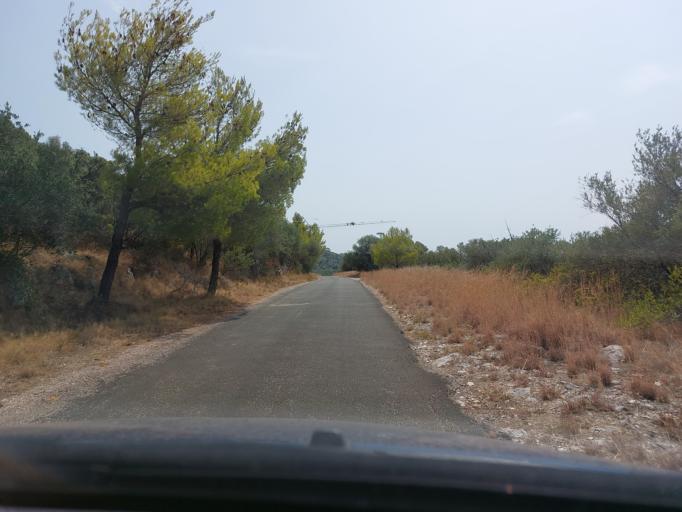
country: HR
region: Dubrovacko-Neretvanska
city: Smokvica
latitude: 42.7367
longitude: 16.8895
